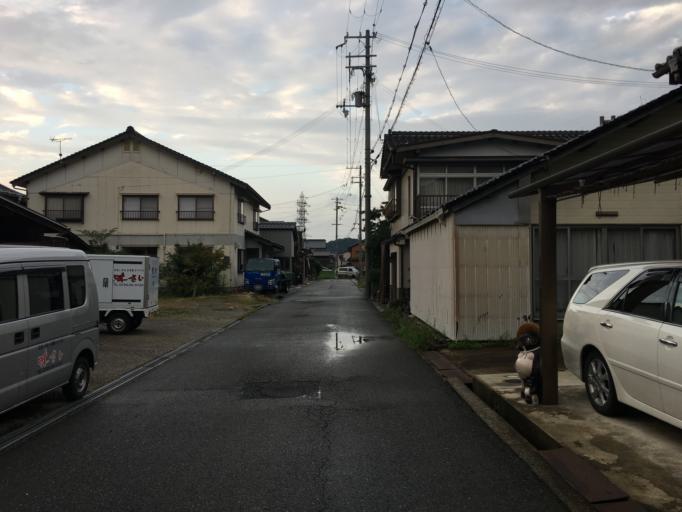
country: JP
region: Hyogo
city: Toyooka
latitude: 35.6337
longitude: 134.6284
